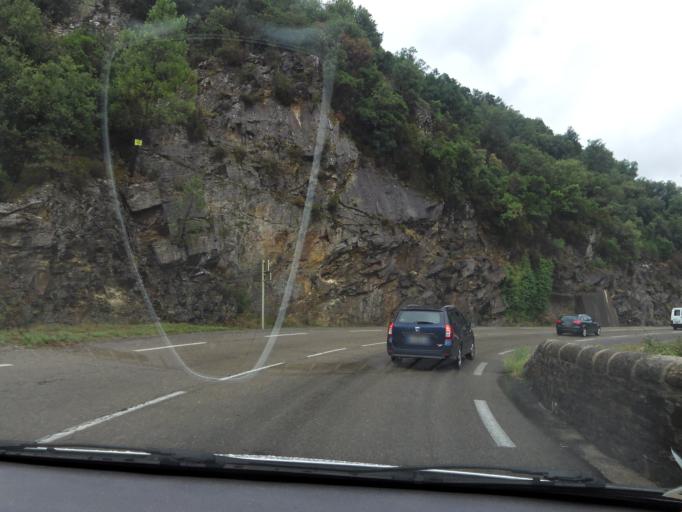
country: FR
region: Languedoc-Roussillon
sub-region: Departement du Gard
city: Branoux-les-Taillades
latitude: 44.2480
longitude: 3.9794
